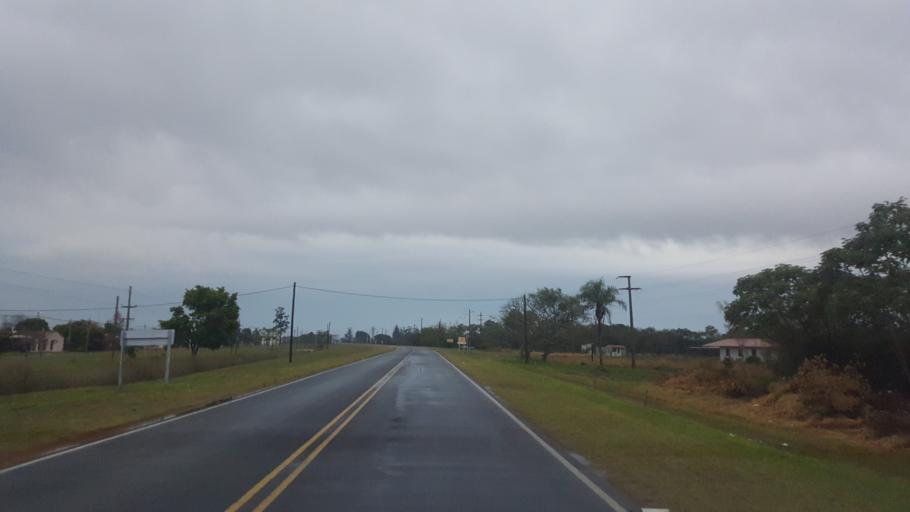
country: AR
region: Corrientes
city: Ituzaingo
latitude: -27.5715
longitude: -56.6684
